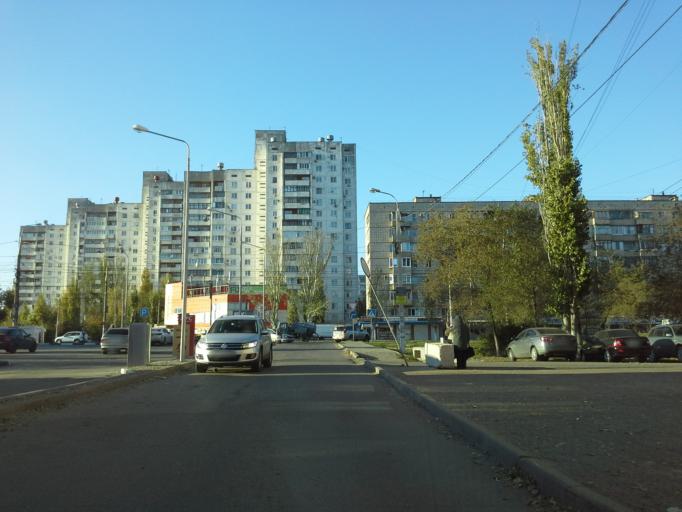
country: RU
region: Volgograd
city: Vodstroy
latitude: 48.8207
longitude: 44.6368
